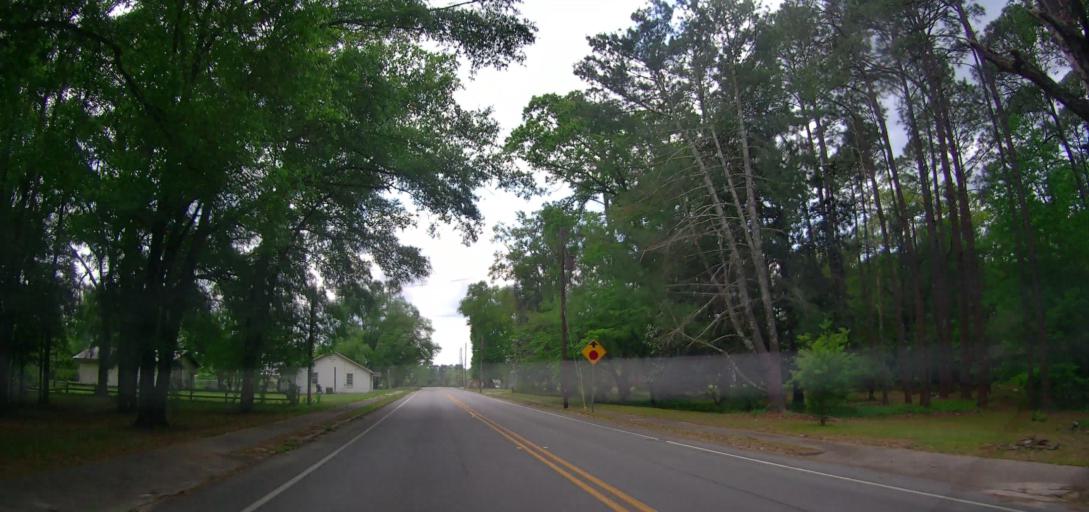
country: US
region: Georgia
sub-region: Treutlen County
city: Soperton
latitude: 32.3762
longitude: -82.5842
